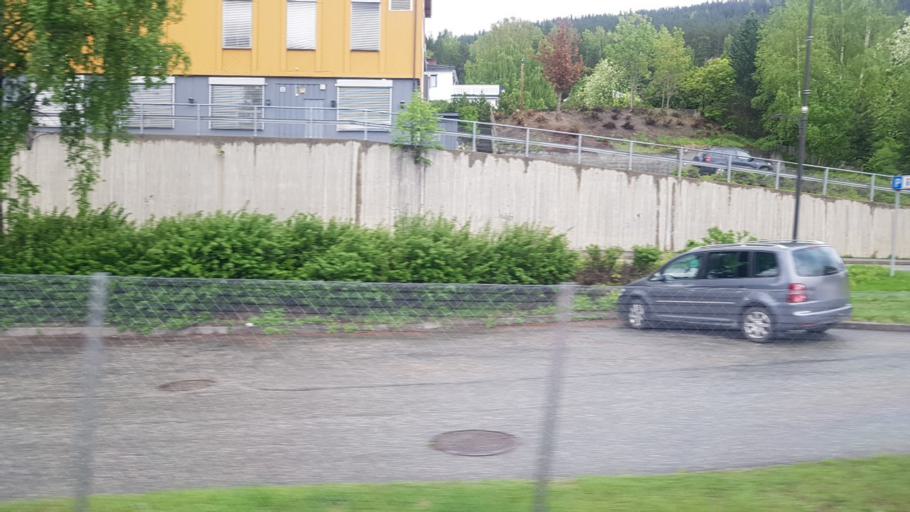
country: NO
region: Oppland
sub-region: Nord-Fron
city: Vinstra
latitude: 61.5963
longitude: 9.7341
